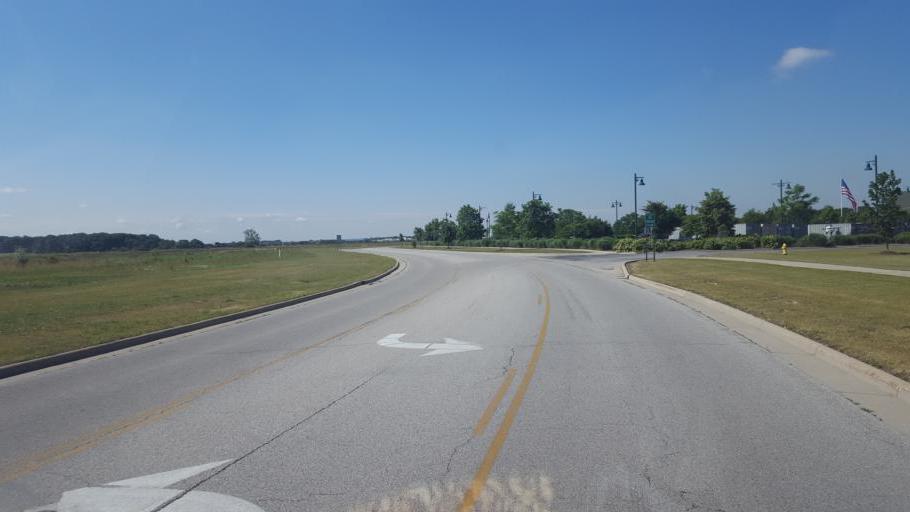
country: US
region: Ohio
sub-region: Wood County
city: Perrysburg
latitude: 41.5619
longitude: -83.5861
